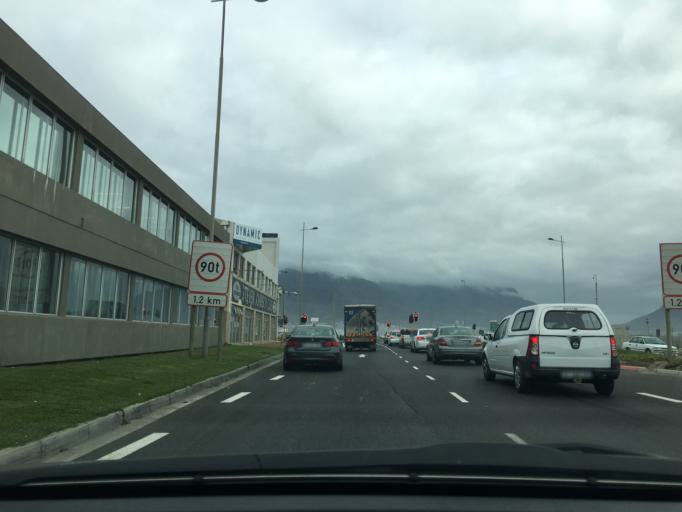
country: ZA
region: Western Cape
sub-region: City of Cape Town
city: Sunset Beach
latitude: -33.8993
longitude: 18.4793
